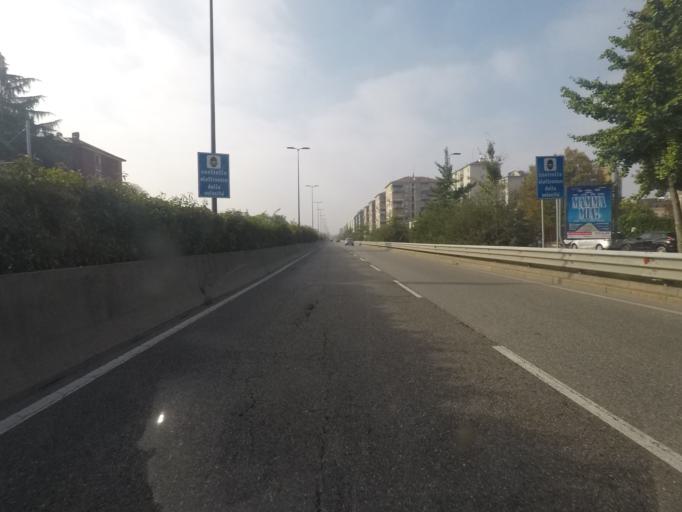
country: IT
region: Lombardy
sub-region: Citta metropolitana di Milano
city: Sesto San Giovanni
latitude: 45.5030
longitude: 9.2449
